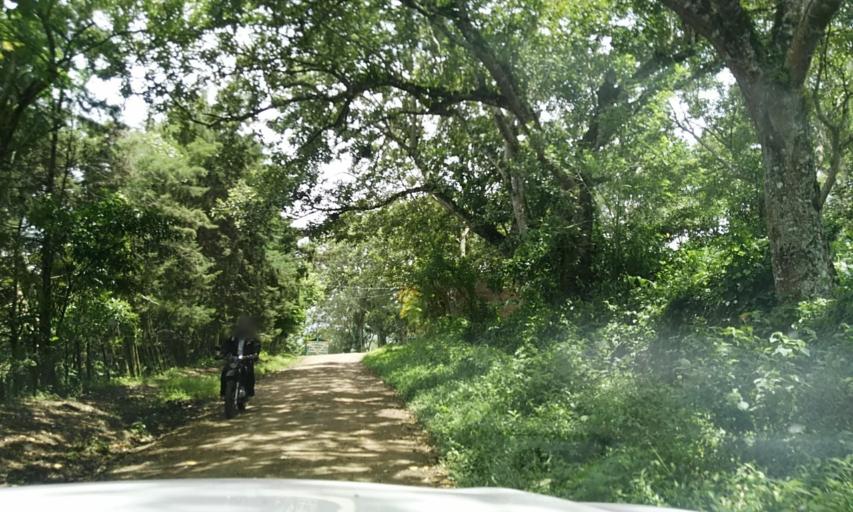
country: NI
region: Matagalpa
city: San Ramon
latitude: 12.9850
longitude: -85.8466
